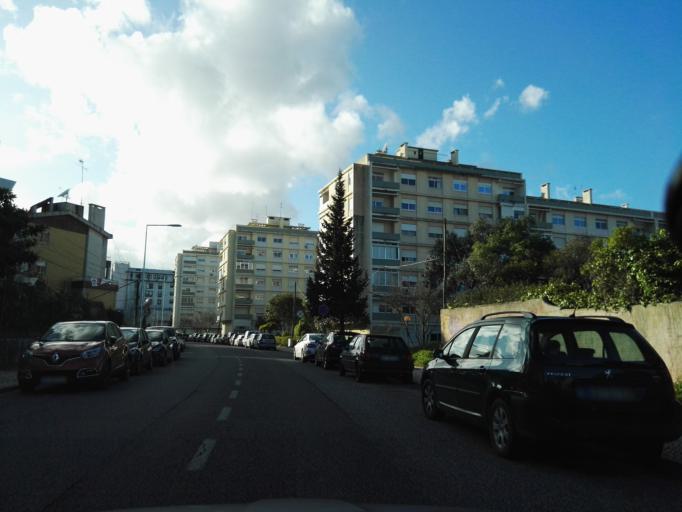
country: PT
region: Lisbon
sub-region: Loures
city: Moscavide
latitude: 38.7673
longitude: -9.1120
